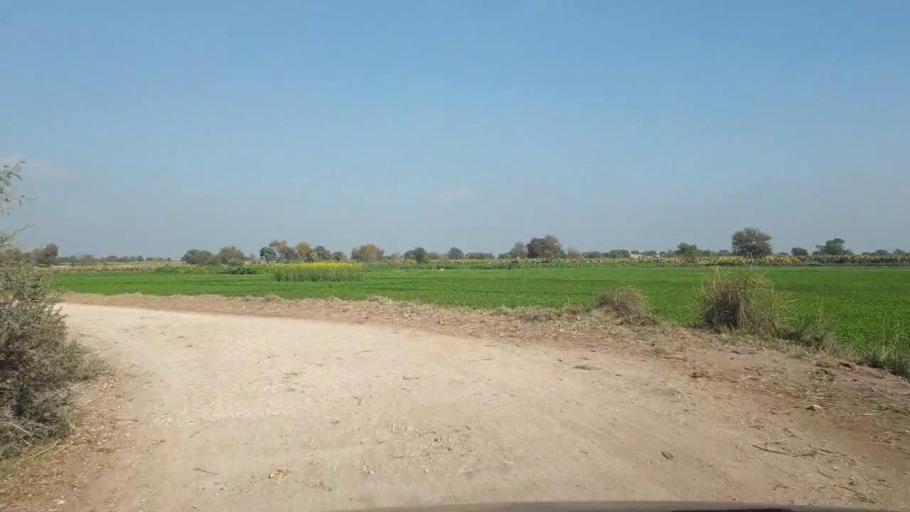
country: PK
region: Sindh
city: Shahdadpur
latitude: 25.9264
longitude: 68.5859
